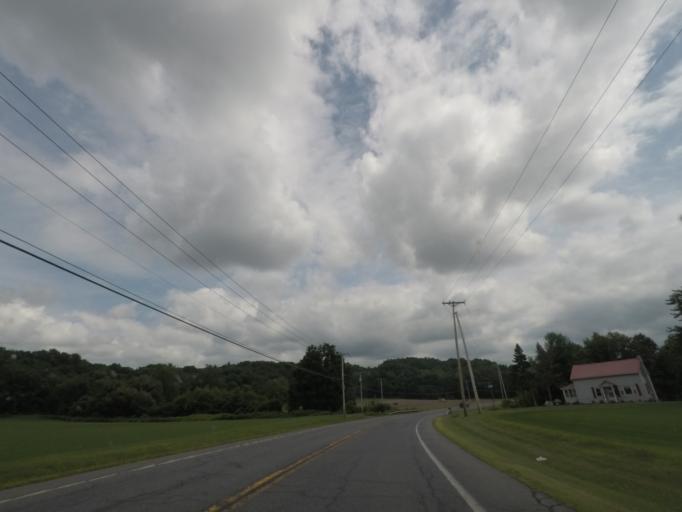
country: US
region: New York
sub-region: Saratoga County
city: Stillwater
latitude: 42.9220
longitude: -73.6320
